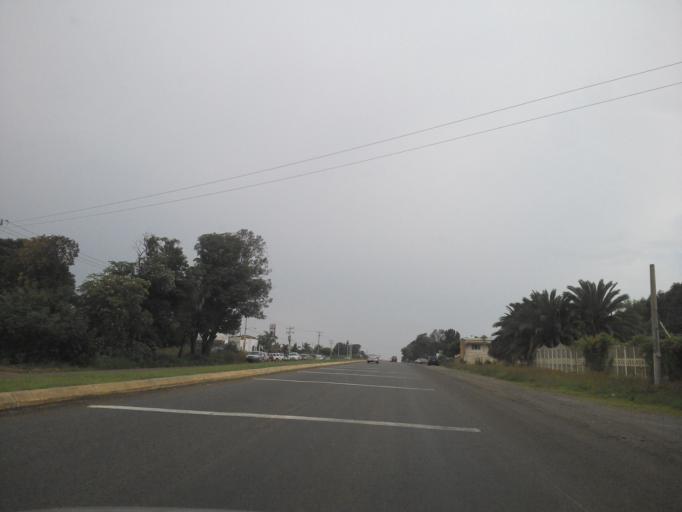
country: MX
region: Jalisco
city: Capilla de Guadalupe
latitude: 20.7809
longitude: -102.5579
